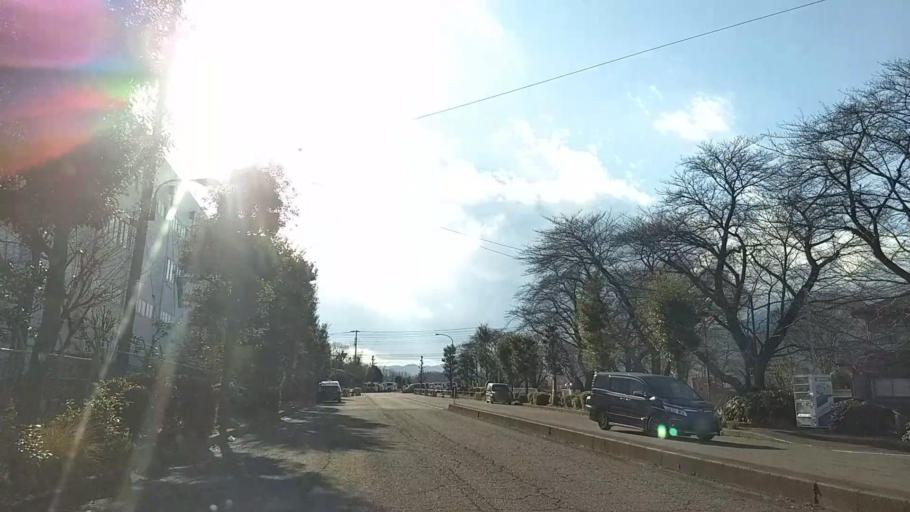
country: JP
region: Kanagawa
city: Atsugi
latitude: 35.4611
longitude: 139.3250
